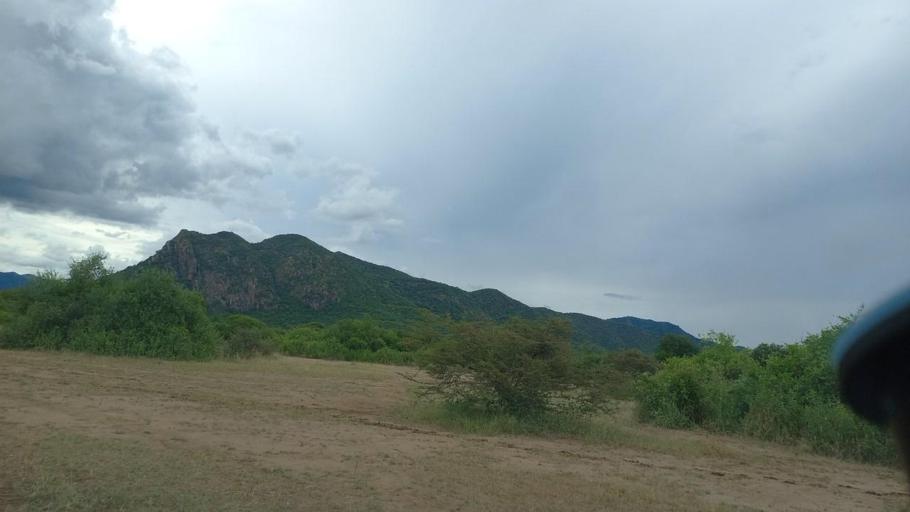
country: ZM
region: Lusaka
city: Luangwa
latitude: -15.6167
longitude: 30.2716
